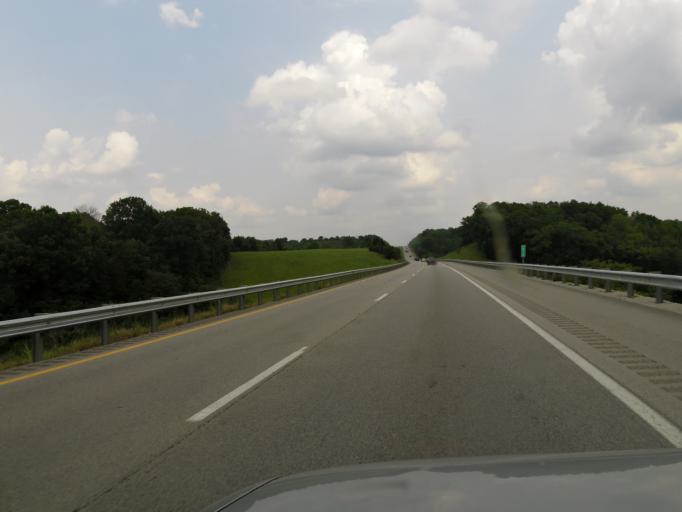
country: US
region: Indiana
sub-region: Switzerland County
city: Vevay
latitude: 38.6754
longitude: -84.9894
